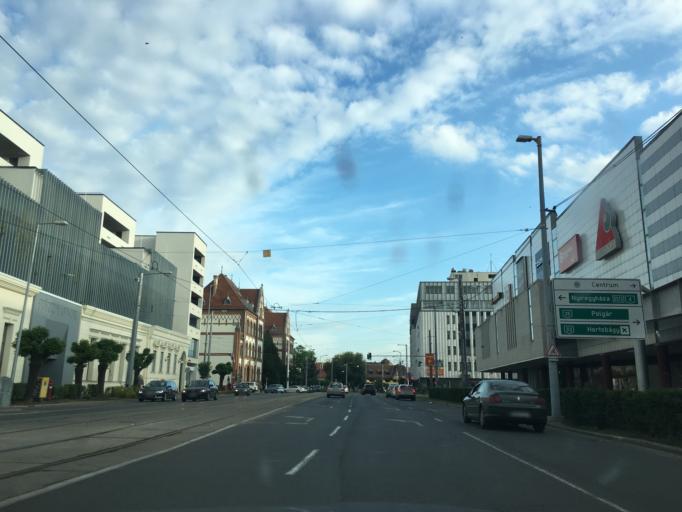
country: HU
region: Hajdu-Bihar
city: Debrecen
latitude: 47.5355
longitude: 21.6259
